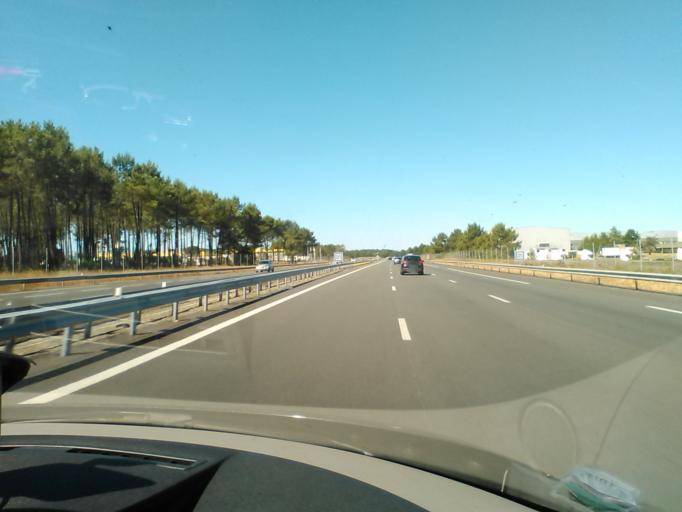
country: FR
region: Aquitaine
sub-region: Departement des Landes
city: Castets
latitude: 43.8705
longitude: -1.1424
